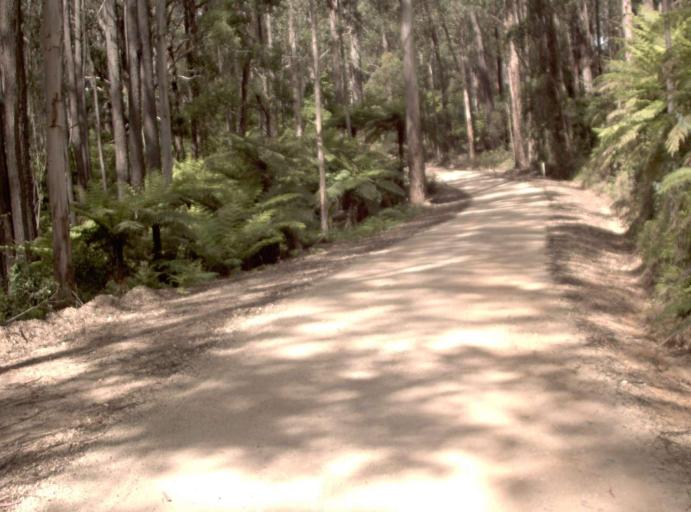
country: AU
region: Victoria
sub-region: East Gippsland
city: Lakes Entrance
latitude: -37.5944
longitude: 148.7173
